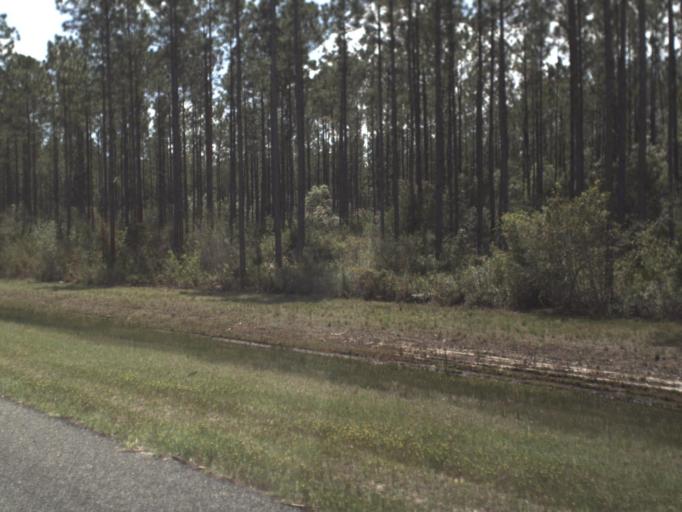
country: US
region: Florida
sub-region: Bay County
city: Laguna Beach
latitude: 30.3809
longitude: -85.8679
